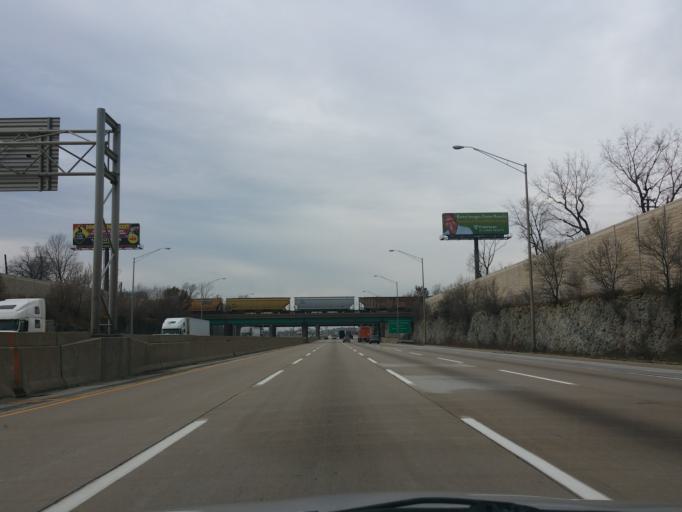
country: US
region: Illinois
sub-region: Cook County
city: Thornton
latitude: 41.5795
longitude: -87.6097
